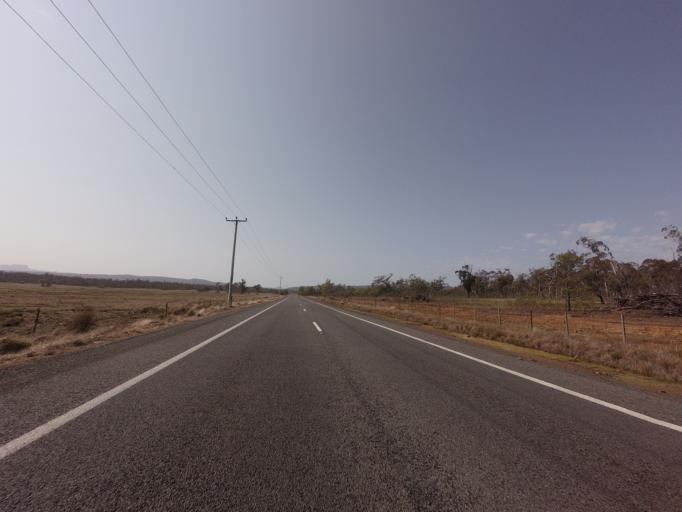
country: AU
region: Tasmania
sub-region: Northern Midlands
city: Evandale
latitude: -41.8328
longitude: 147.4712
